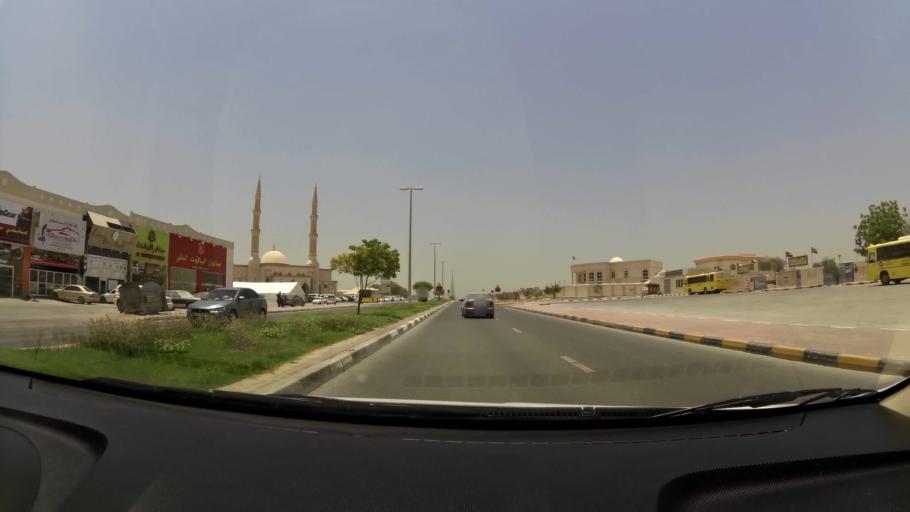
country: AE
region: Ajman
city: Ajman
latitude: 25.4038
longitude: 55.4974
